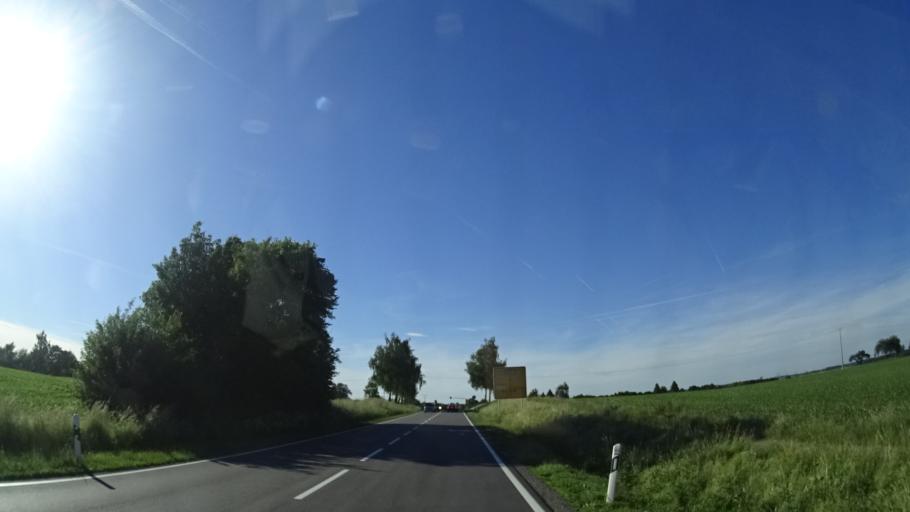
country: DE
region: Baden-Wuerttemberg
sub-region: Regierungsbezirk Stuttgart
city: Kupferzell
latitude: 49.1936
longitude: 9.6922
